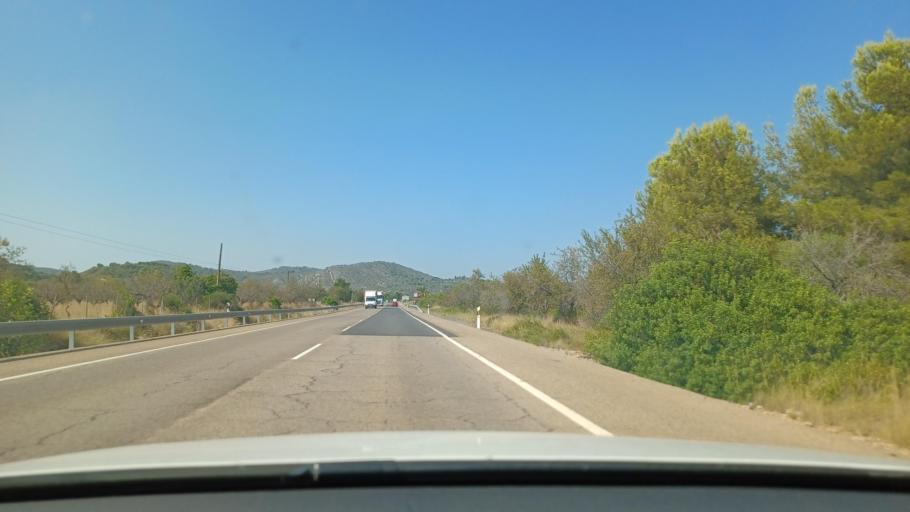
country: ES
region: Valencia
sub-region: Provincia de Castello
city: Alcala de Xivert
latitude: 40.2582
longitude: 0.2375
